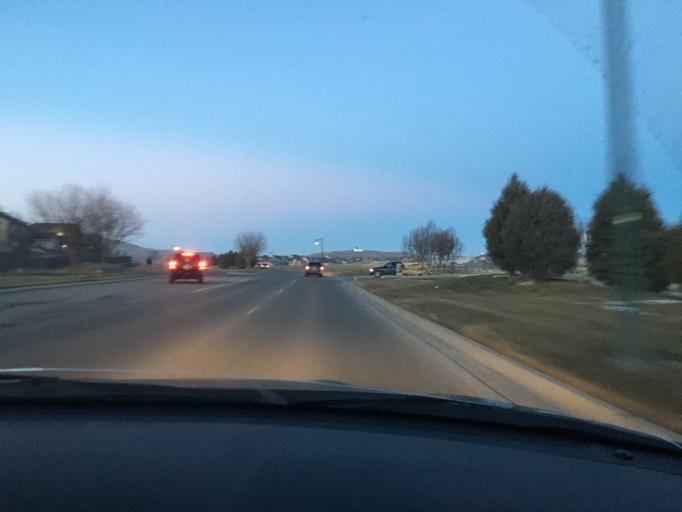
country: US
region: Utah
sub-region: Utah County
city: Eagle Mountain
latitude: 40.3712
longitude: -111.9747
